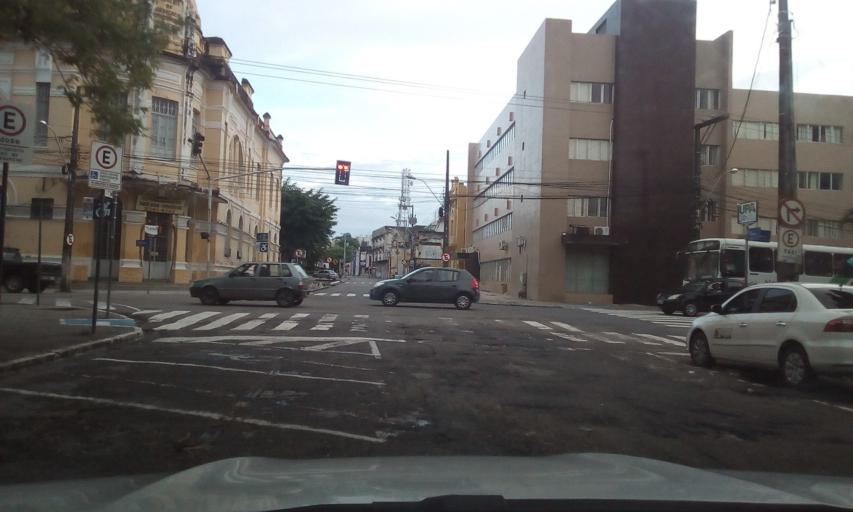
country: BR
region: Paraiba
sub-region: Joao Pessoa
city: Joao Pessoa
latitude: -7.1225
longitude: -34.8844
